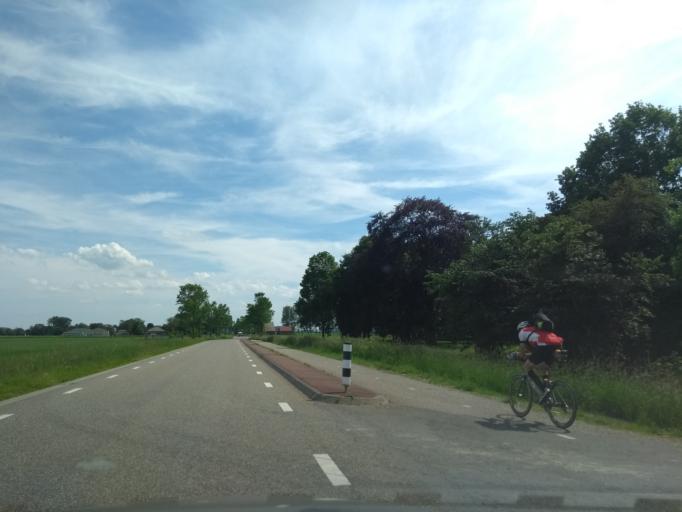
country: NL
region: Groningen
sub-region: Gemeente Zuidhorn
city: Noordhorn
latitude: 53.2802
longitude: 6.4231
